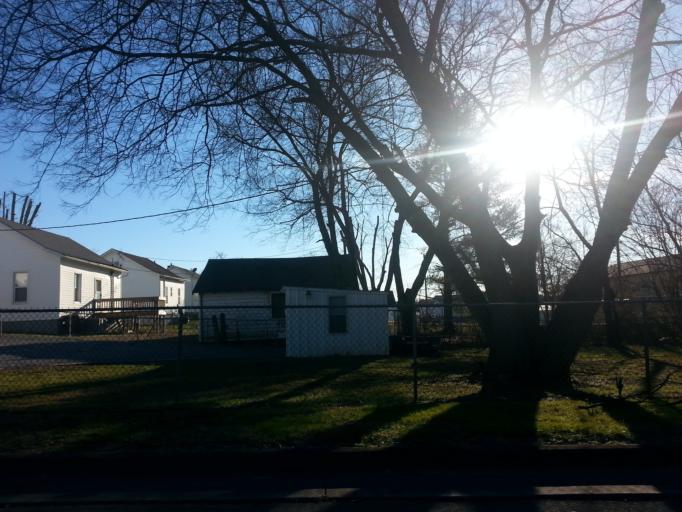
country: US
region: Tennessee
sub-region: Blount County
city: Maryville
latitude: 35.7612
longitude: -83.9720
